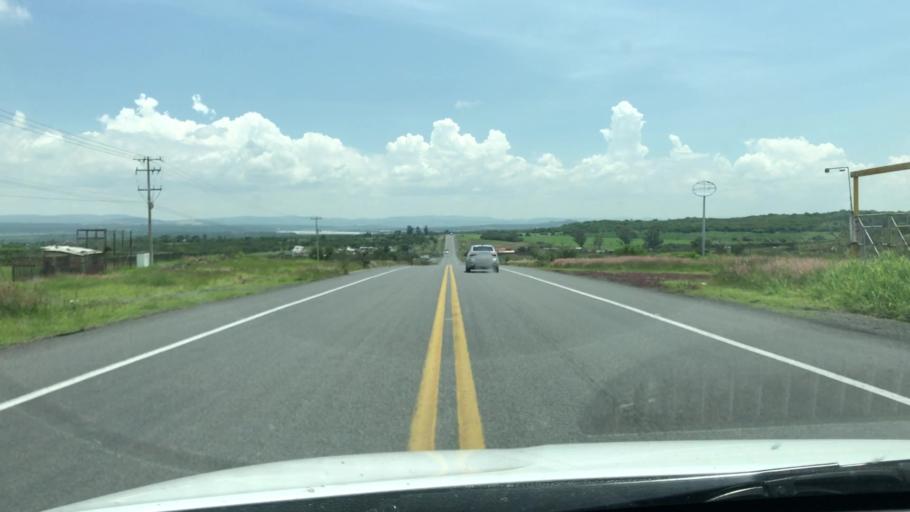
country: MX
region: Jalisco
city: Degollado
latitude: 20.3500
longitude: -102.1565
